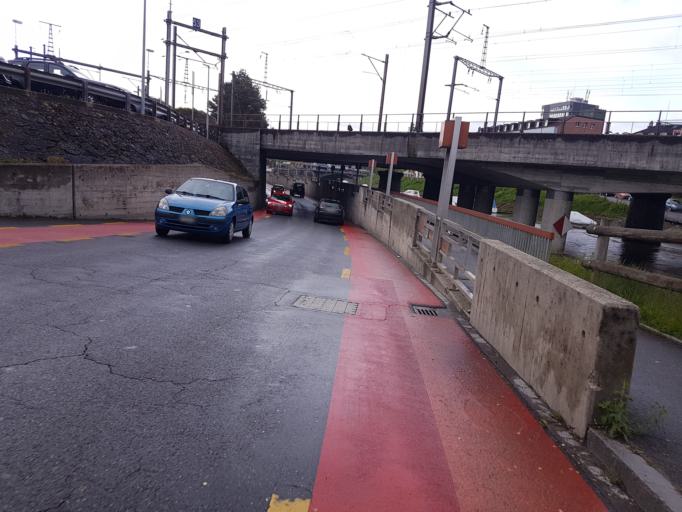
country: CH
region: Vaud
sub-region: Jura-Nord vaudois District
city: Yverdon-les-Bains
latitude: 46.7833
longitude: 6.6372
